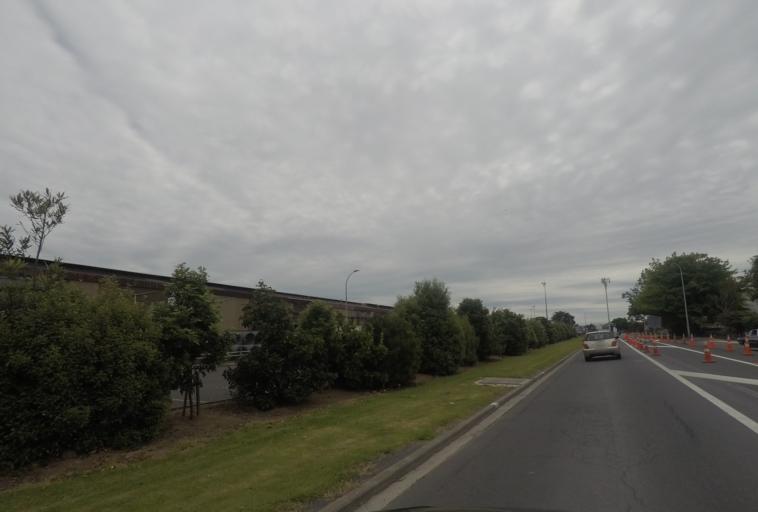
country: NZ
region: Auckland
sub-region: Auckland
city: Mangere
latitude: -36.9486
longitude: 174.8238
